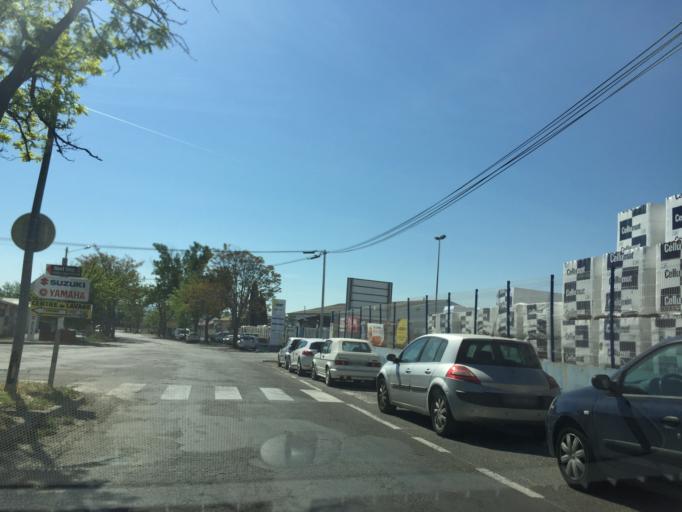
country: FR
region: Provence-Alpes-Cote d'Azur
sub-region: Departement des Alpes-de-Haute-Provence
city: Manosque
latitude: 43.8213
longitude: 5.7978
